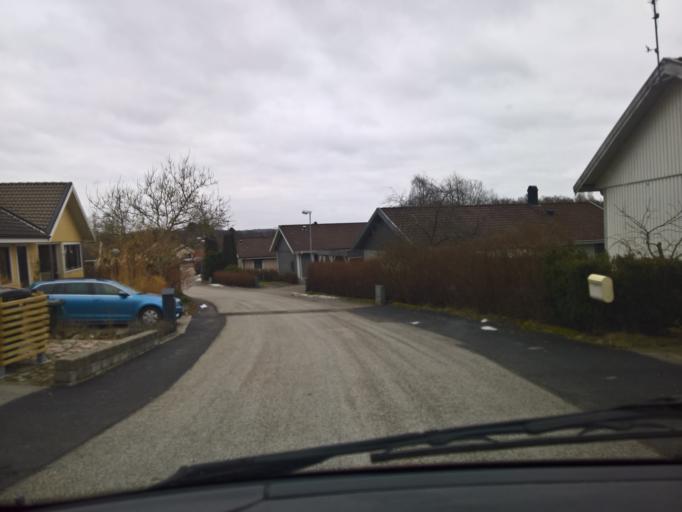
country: SE
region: Skane
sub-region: Hoors Kommun
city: Hoeoer
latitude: 55.9251
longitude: 13.5310
